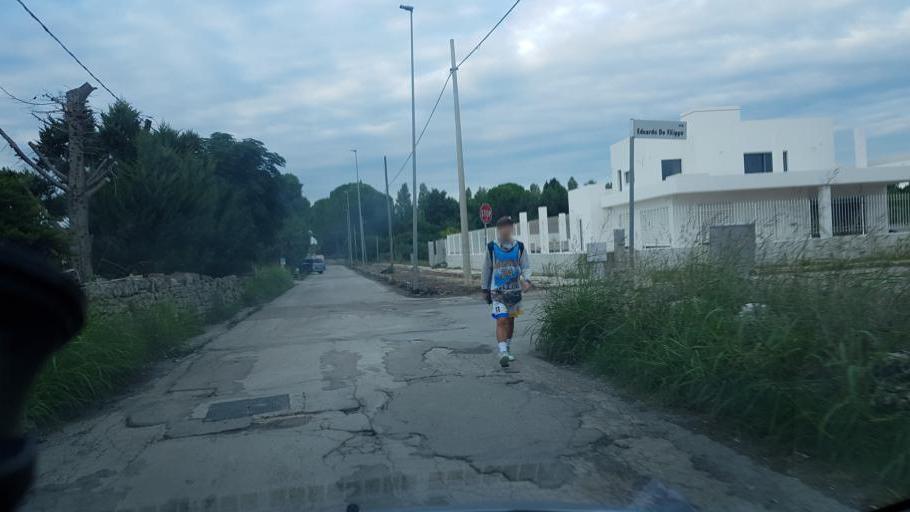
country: IT
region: Apulia
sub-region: Provincia di Brindisi
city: Oria
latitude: 40.5047
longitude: 17.6434
